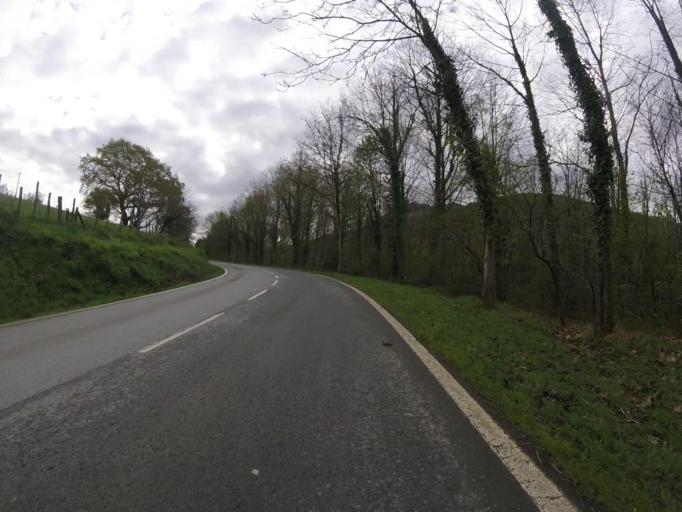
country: ES
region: Navarre
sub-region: Provincia de Navarra
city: Etxalar
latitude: 43.2832
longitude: -1.6354
